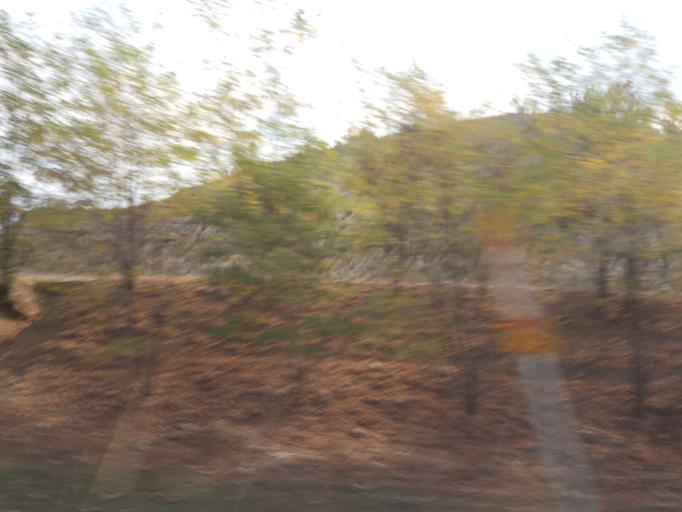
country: TR
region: Sinop
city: Sarayduzu
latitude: 41.3833
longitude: 34.9159
